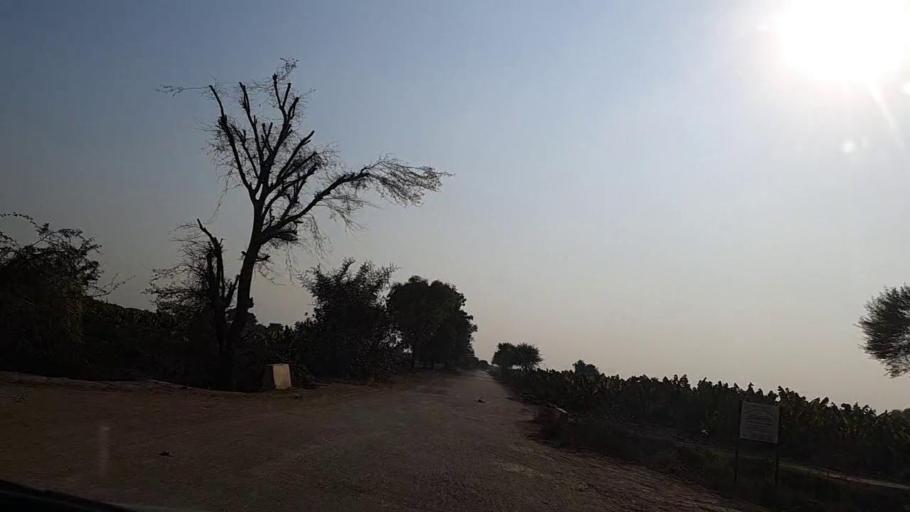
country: PK
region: Sindh
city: Sakrand
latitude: 26.0759
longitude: 68.2633
